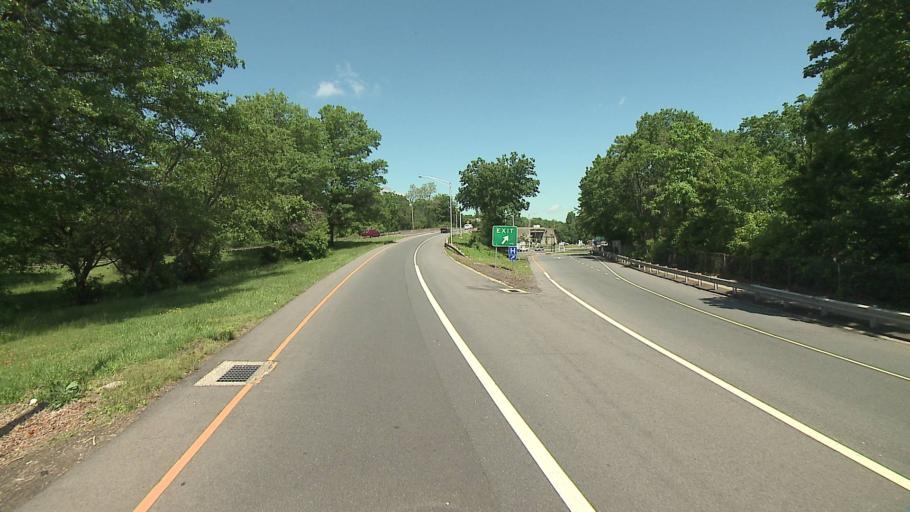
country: US
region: Connecticut
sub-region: Fairfield County
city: Norwalk
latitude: 41.1078
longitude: -73.4176
